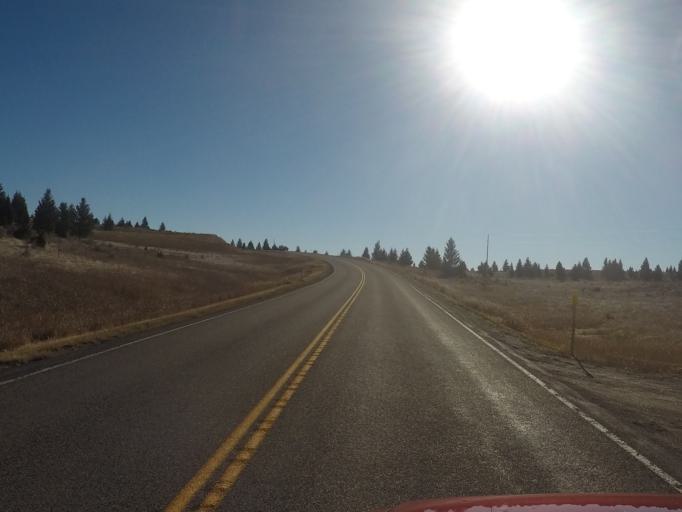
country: US
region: Montana
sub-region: Meagher County
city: White Sulphur Springs
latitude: 46.3521
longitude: -111.0758
